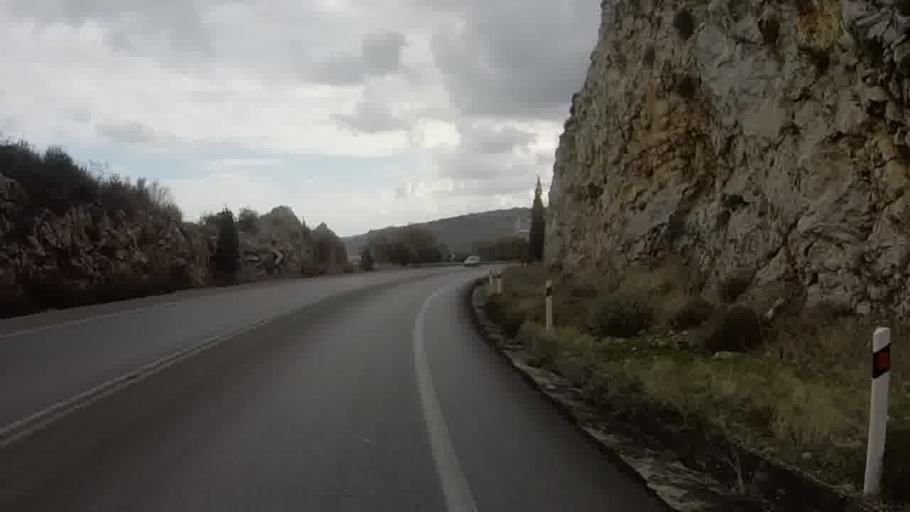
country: GR
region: Crete
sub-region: Nomos Rethymnis
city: Atsipopoulon
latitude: 35.3605
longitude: 24.3816
